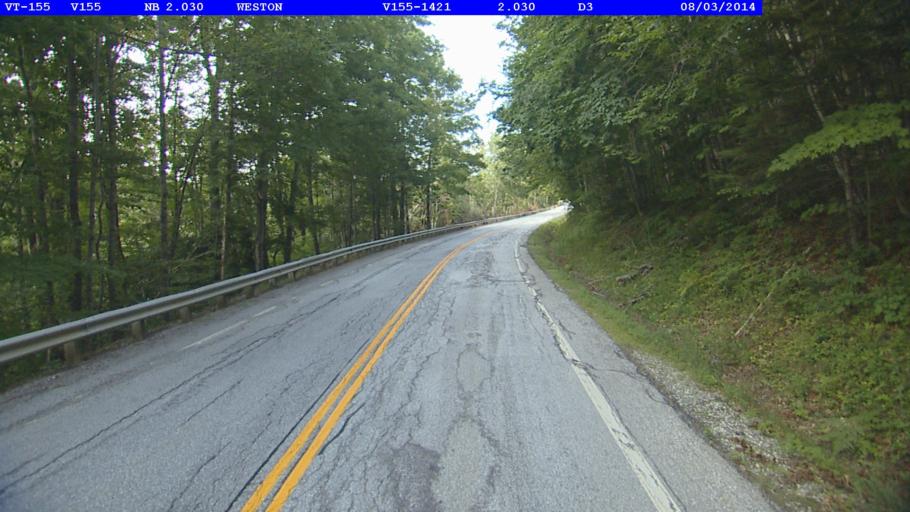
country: US
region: Vermont
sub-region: Windsor County
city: Chester
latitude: 43.3645
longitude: -72.7936
